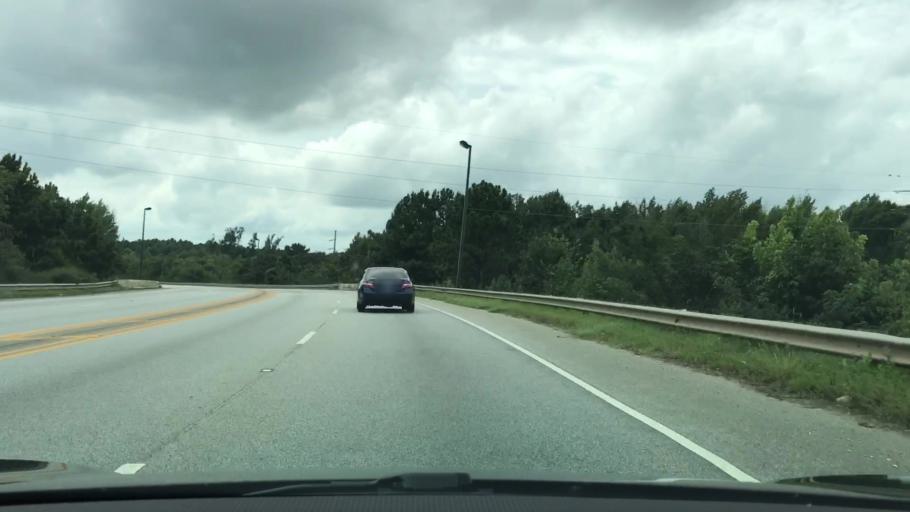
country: US
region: Alabama
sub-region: Lee County
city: Opelika
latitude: 32.6334
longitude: -85.4093
